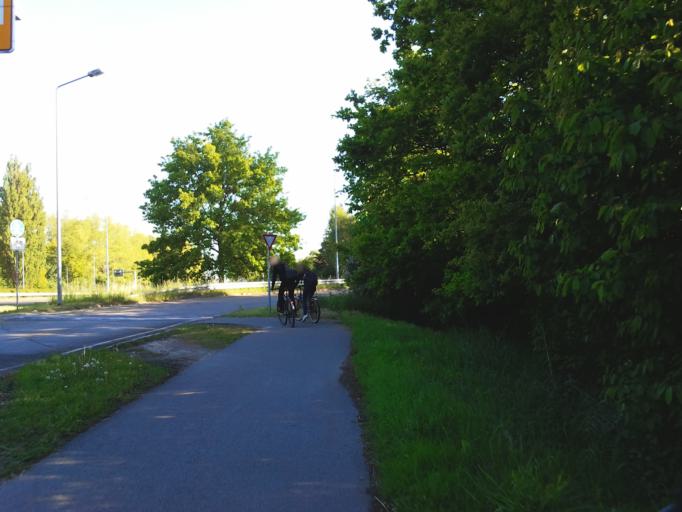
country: DE
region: Mecklenburg-Vorpommern
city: Warnemuende
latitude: 54.1372
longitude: 12.0628
